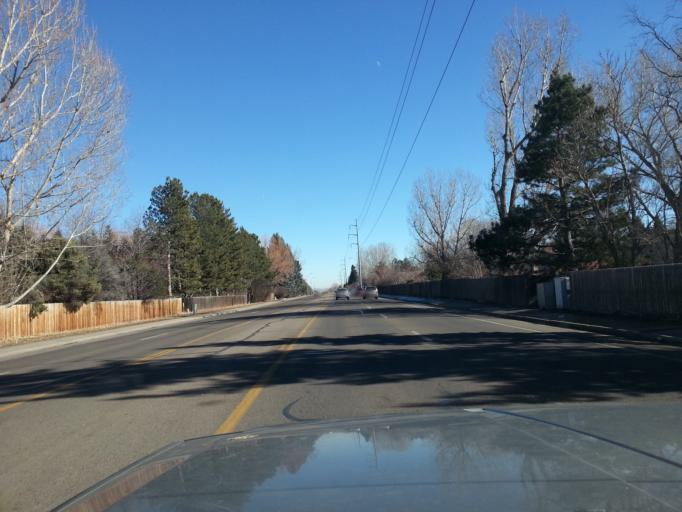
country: US
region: Colorado
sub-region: Larimer County
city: Fort Collins
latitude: 40.5526
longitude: -105.0517
